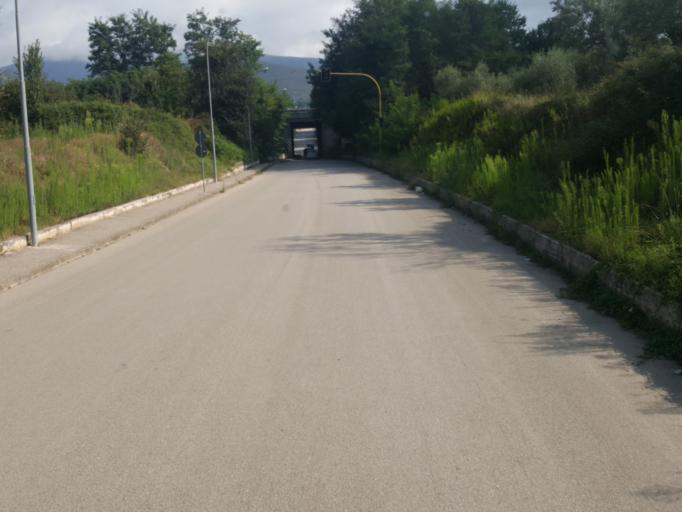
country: IT
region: Campania
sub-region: Provincia di Caserta
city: Pignataro Maggiore
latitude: 41.1832
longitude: 14.1591
